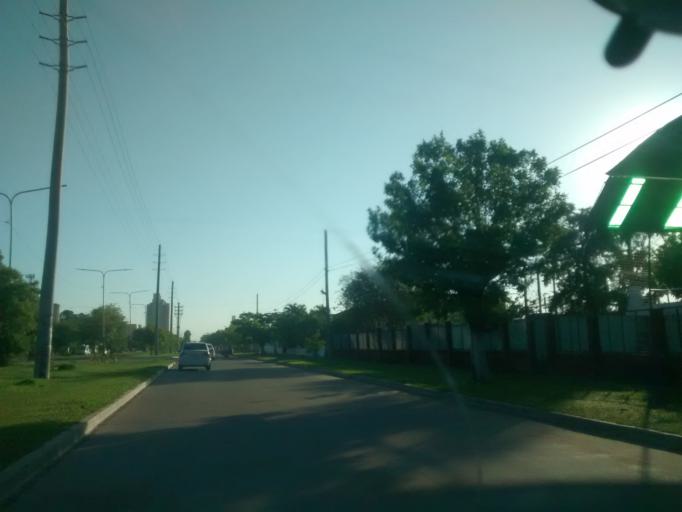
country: AR
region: Chaco
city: Resistencia
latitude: -27.4685
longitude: -58.9916
